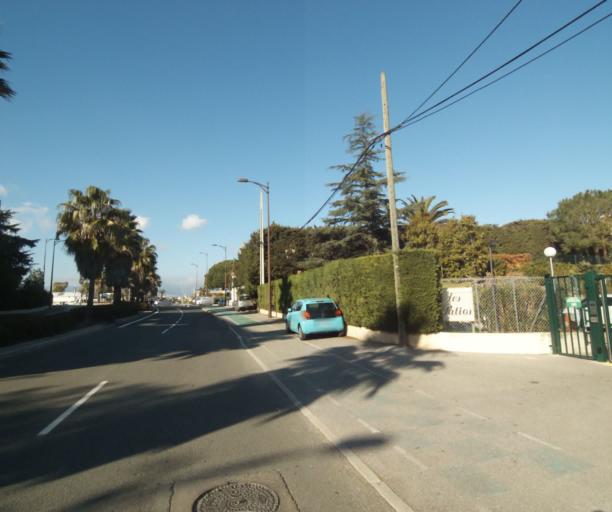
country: FR
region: Provence-Alpes-Cote d'Azur
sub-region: Departement des Alpes-Maritimes
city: Biot
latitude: 43.5960
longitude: 7.1144
